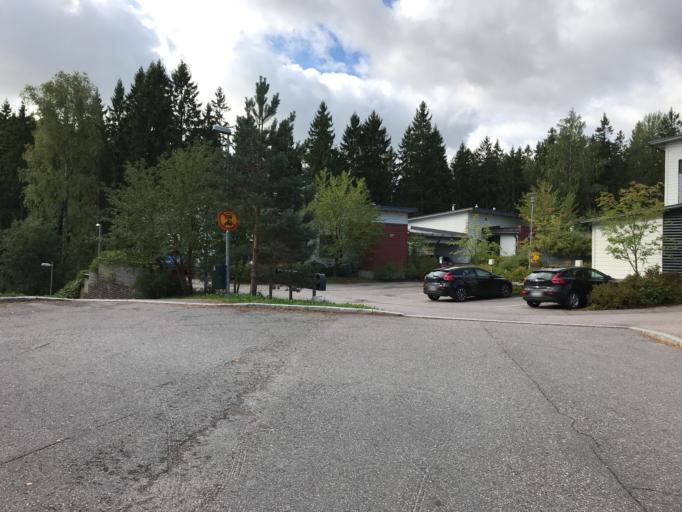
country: FI
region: Uusimaa
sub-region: Helsinki
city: Vantaa
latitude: 60.2241
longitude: 25.0491
